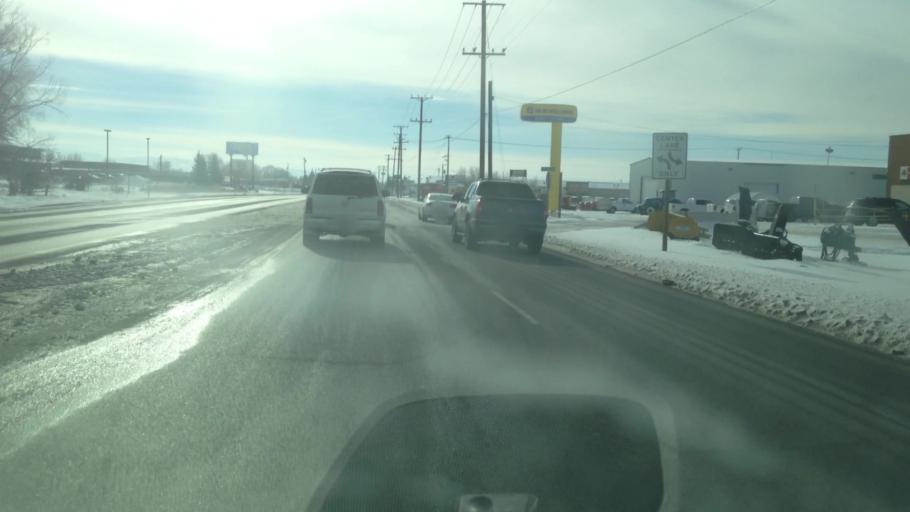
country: US
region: Idaho
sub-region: Bonneville County
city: Idaho Falls
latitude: 43.5249
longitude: -112.0236
